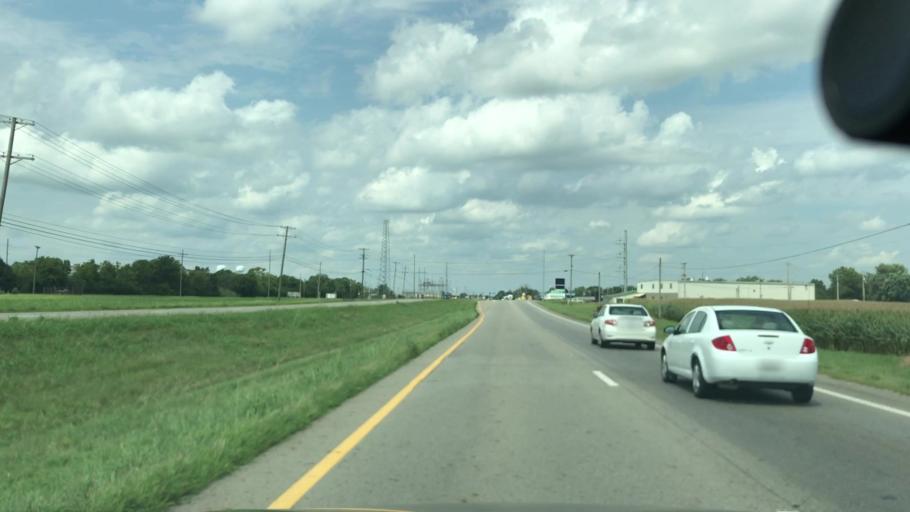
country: US
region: Ohio
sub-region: Pickaway County
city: Logan Elm Village
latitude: 39.5605
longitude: -82.9574
